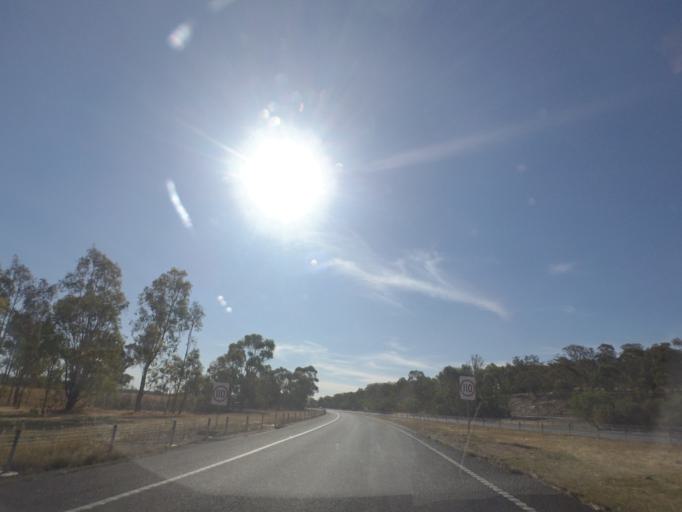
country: AU
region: Victoria
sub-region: Murrindindi
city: Kinglake West
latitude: -36.9840
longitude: 145.1388
